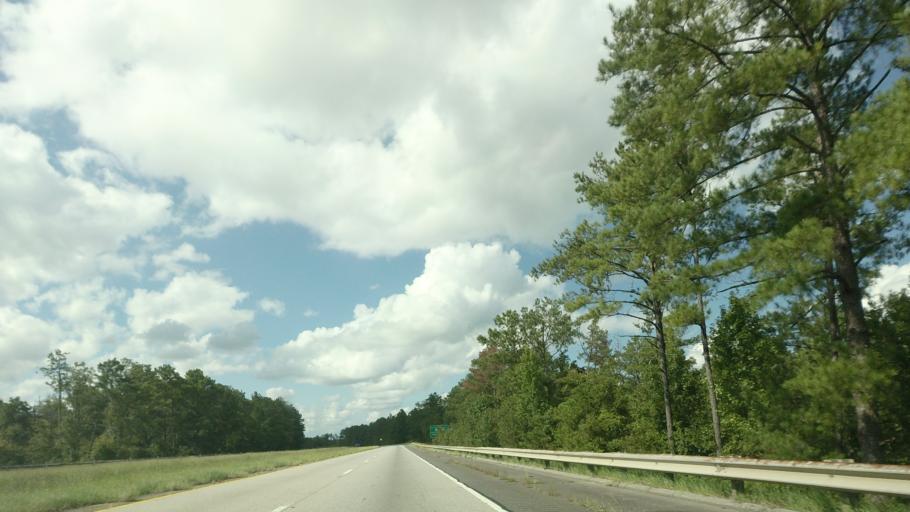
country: US
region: Georgia
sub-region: Bibb County
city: Macon
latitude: 32.7826
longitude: -83.5589
